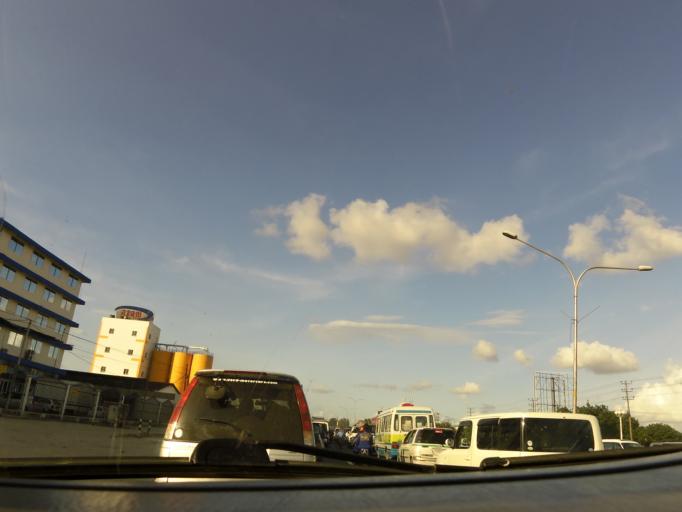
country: TZ
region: Dar es Salaam
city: Dar es Salaam
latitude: -6.8449
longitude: 39.2435
